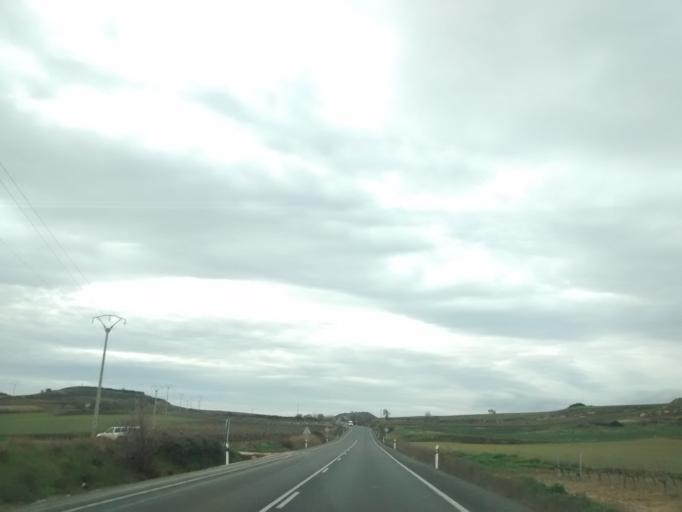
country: ES
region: La Rioja
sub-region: Provincia de La Rioja
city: Briones
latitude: 42.5477
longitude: -2.8005
